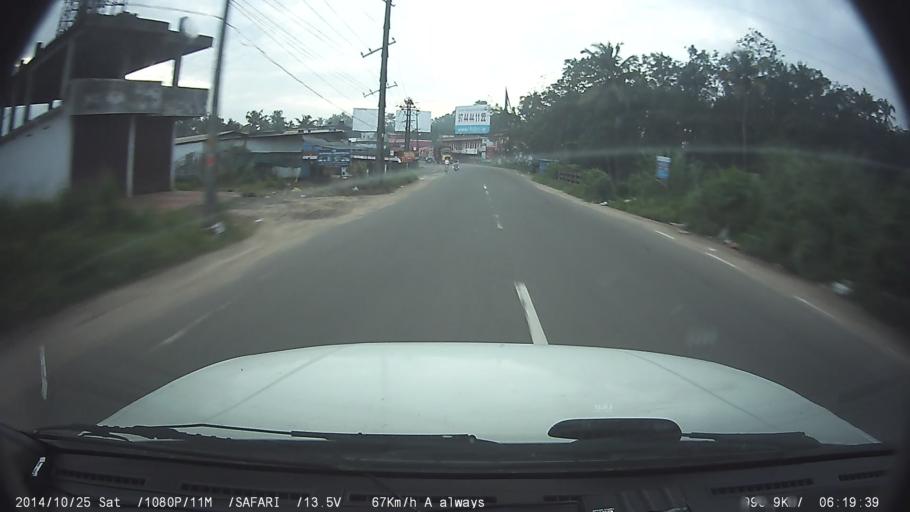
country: IN
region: Kerala
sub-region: Ernakulam
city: Perumbavoor
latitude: 10.1061
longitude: 76.4822
